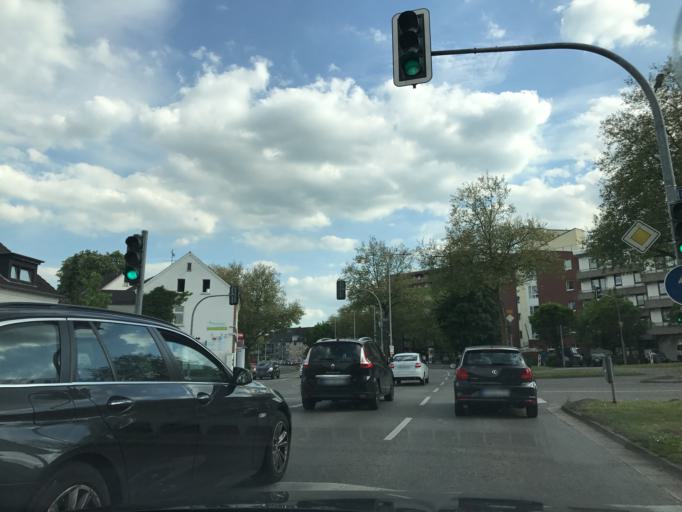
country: DE
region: North Rhine-Westphalia
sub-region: Regierungsbezirk Dusseldorf
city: Muelheim (Ruhr)
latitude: 51.4083
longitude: 6.8690
